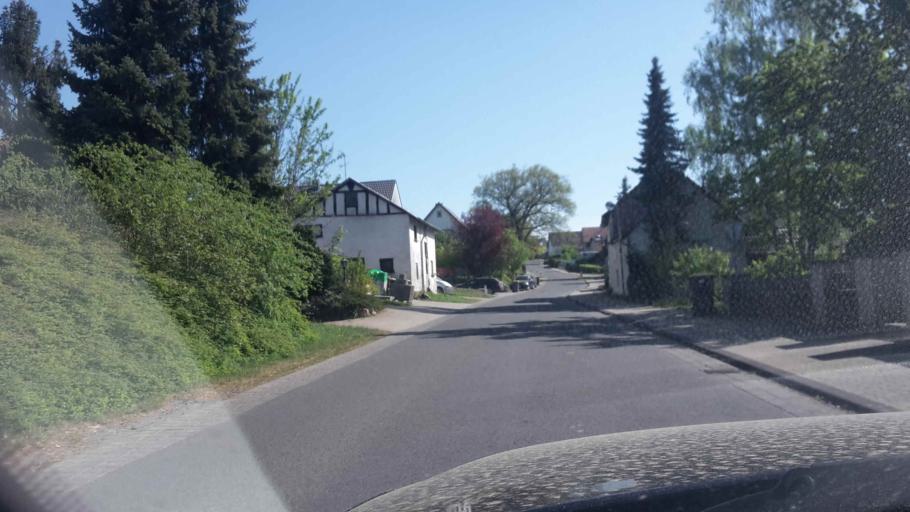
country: DE
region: Rheinland-Pfalz
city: Windhagen
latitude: 50.6685
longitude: 7.3376
